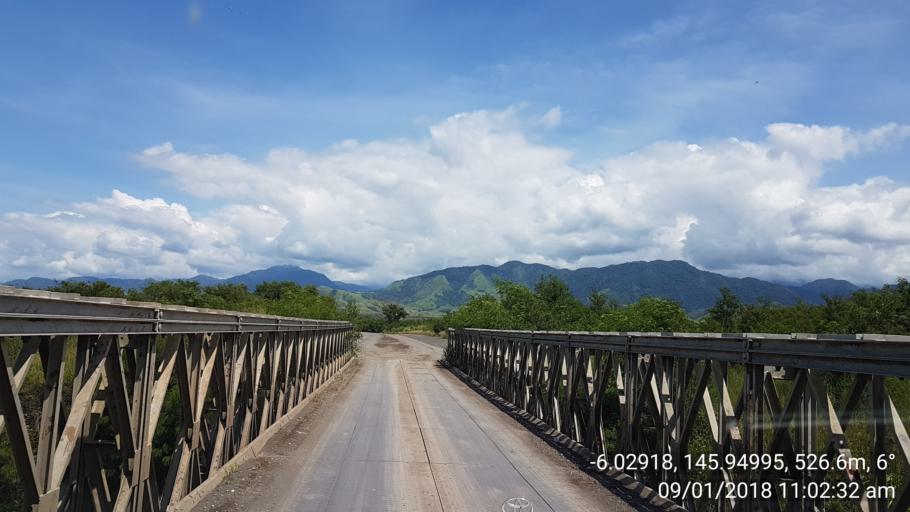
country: PG
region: Eastern Highlands
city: Kainantu
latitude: -6.0292
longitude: 145.9500
